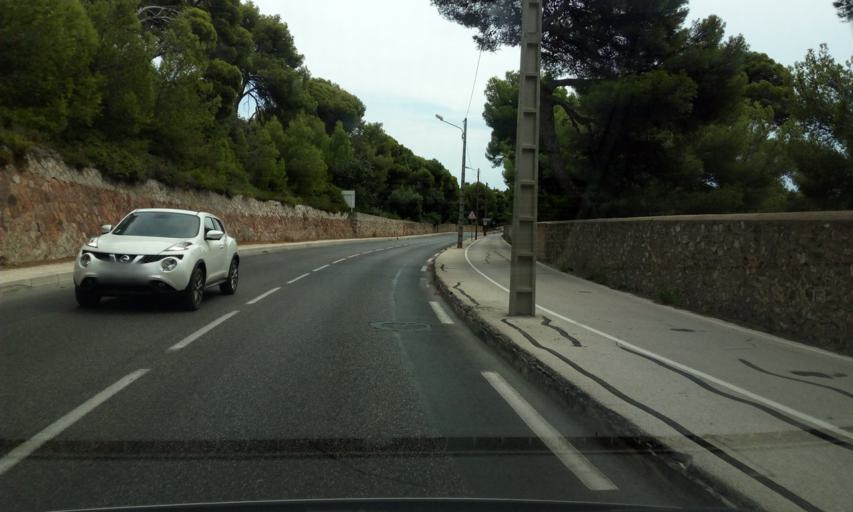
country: FR
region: Provence-Alpes-Cote d'Azur
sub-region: Departement du Var
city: Carqueiranne
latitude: 43.0839
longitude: 6.1143
